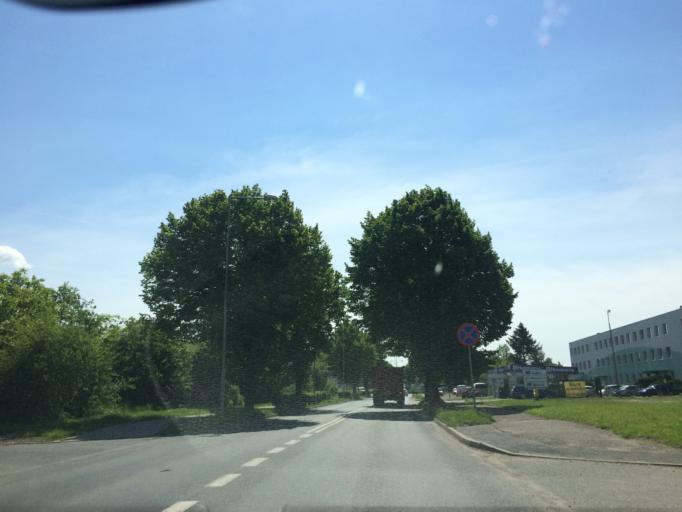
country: PL
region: Lower Silesian Voivodeship
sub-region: Powiat swidnicki
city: Swidnica
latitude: 50.8343
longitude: 16.5029
